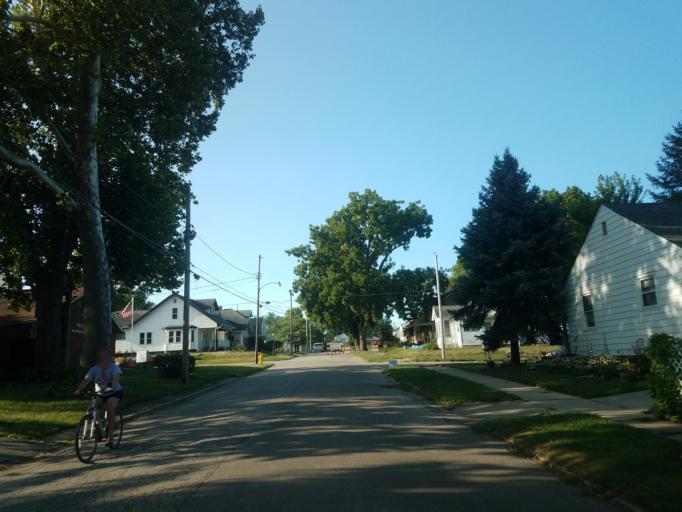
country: US
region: Illinois
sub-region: McLean County
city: Bloomington
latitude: 40.4758
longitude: -88.9780
